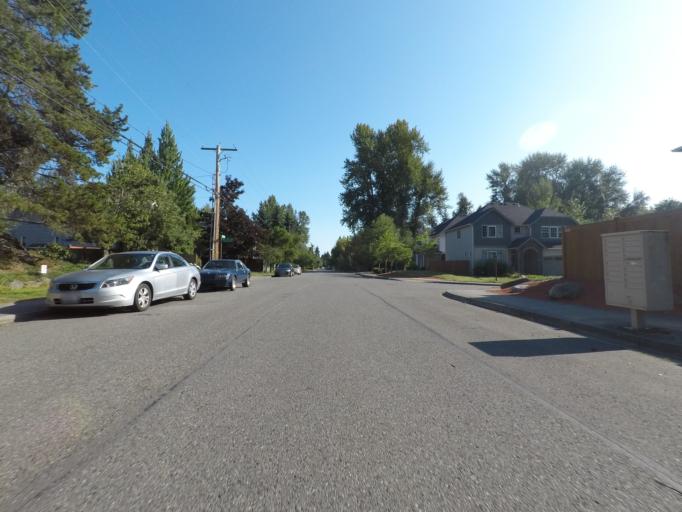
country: US
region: Washington
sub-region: King County
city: Inglewood-Finn Hill
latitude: 47.7378
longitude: -122.2373
